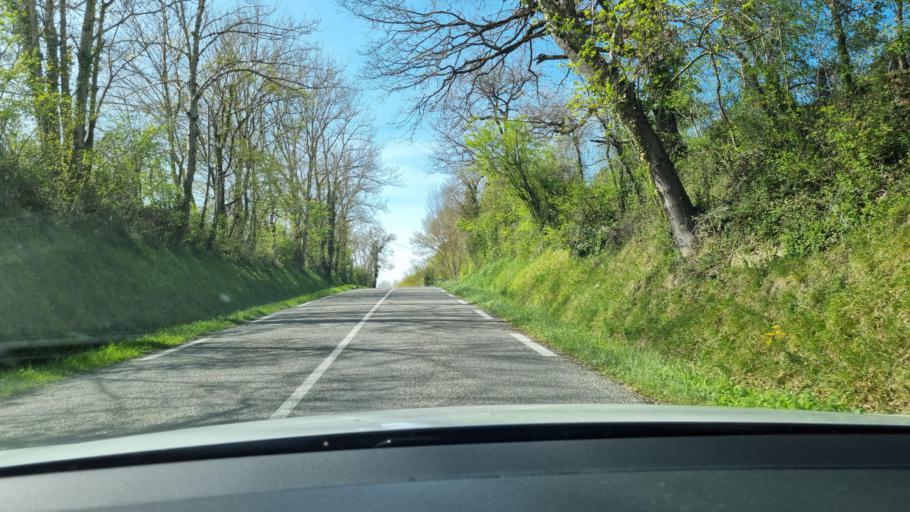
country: FR
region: Midi-Pyrenees
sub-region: Departement du Gers
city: Samatan
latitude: 43.4889
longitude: 1.0154
